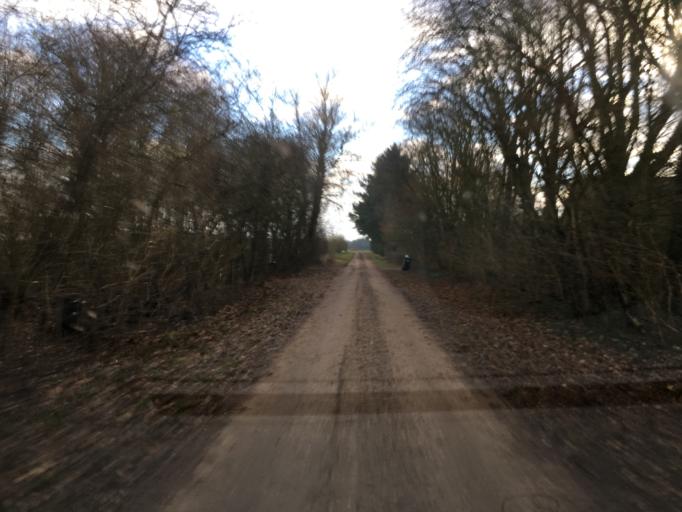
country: DK
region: South Denmark
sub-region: Tonder Kommune
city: Sherrebek
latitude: 55.1335
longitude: 8.8655
